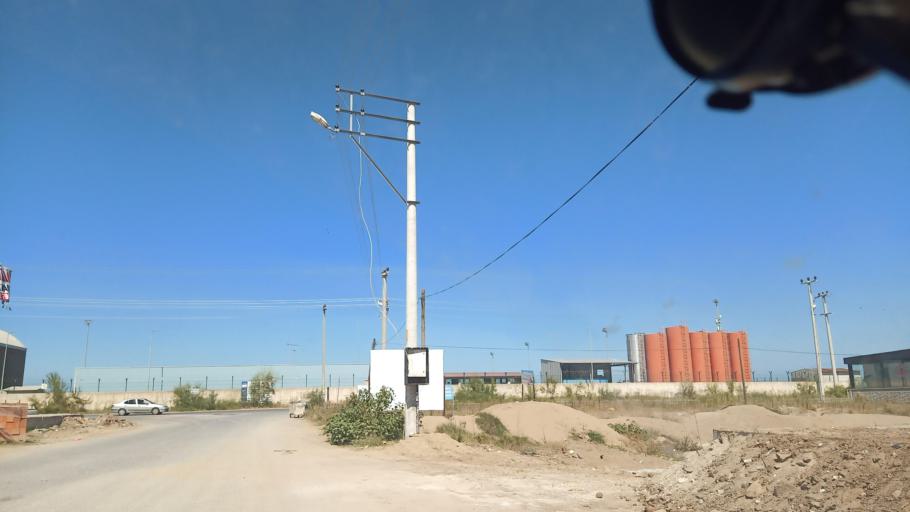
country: TR
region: Sakarya
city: Karasu
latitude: 41.1164
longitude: 30.6739
